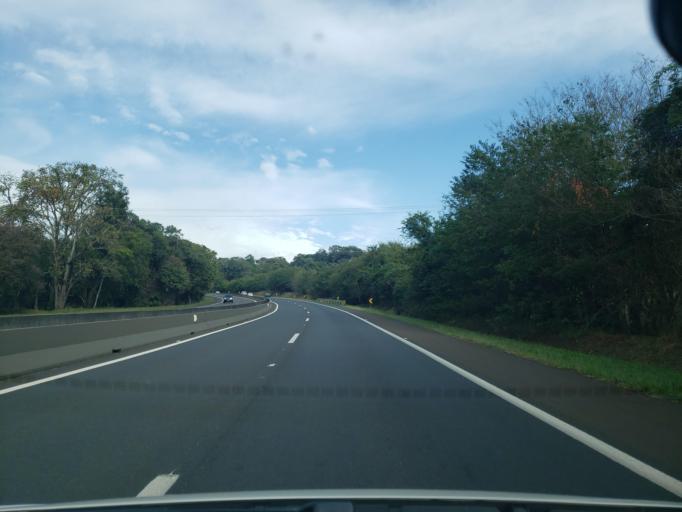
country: BR
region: Sao Paulo
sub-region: Brotas
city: Brotas
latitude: -22.2772
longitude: -47.9834
